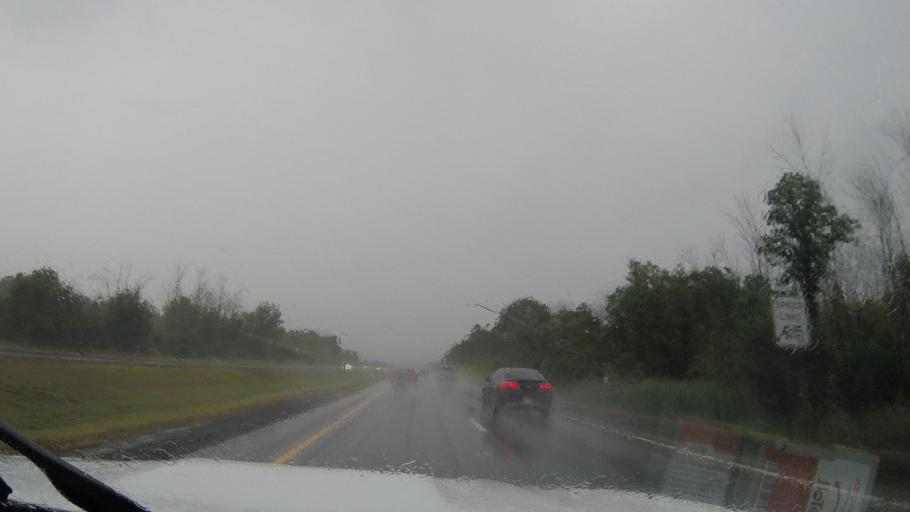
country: US
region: New York
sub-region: Seneca County
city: Waterloo
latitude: 42.9604
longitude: -76.8991
